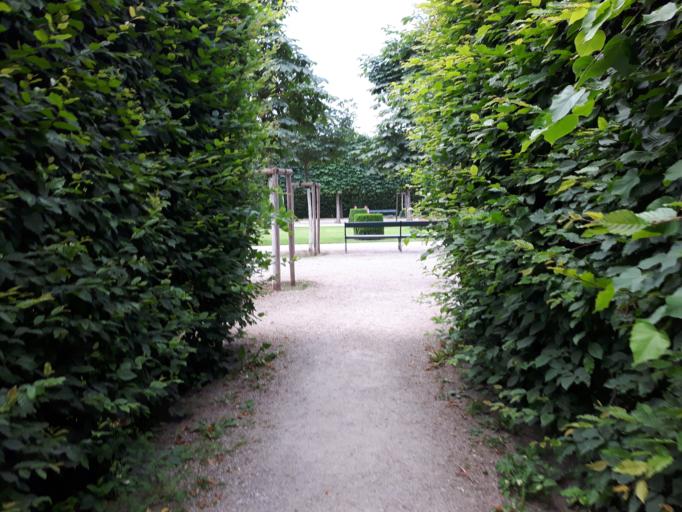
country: AT
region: Vienna
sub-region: Wien Stadt
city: Vienna
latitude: 48.1859
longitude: 16.3093
